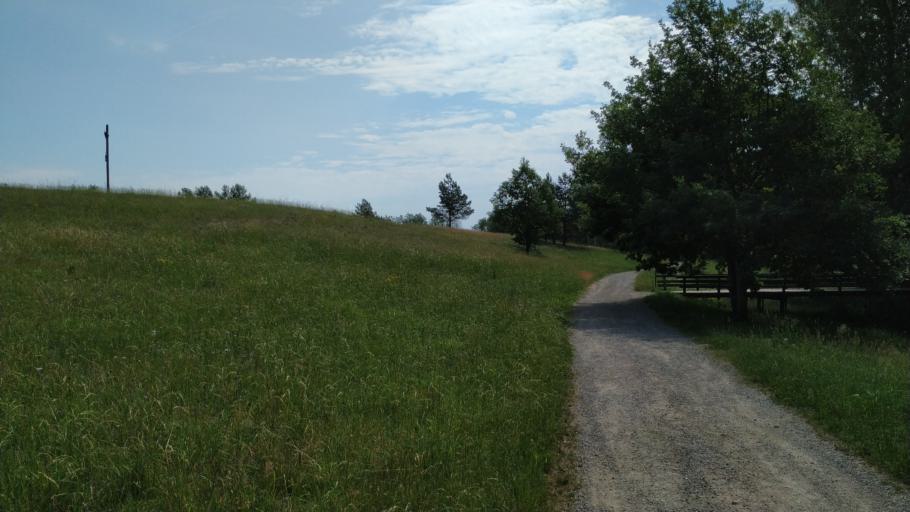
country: LT
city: Nemencine
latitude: 54.9075
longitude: 25.3198
